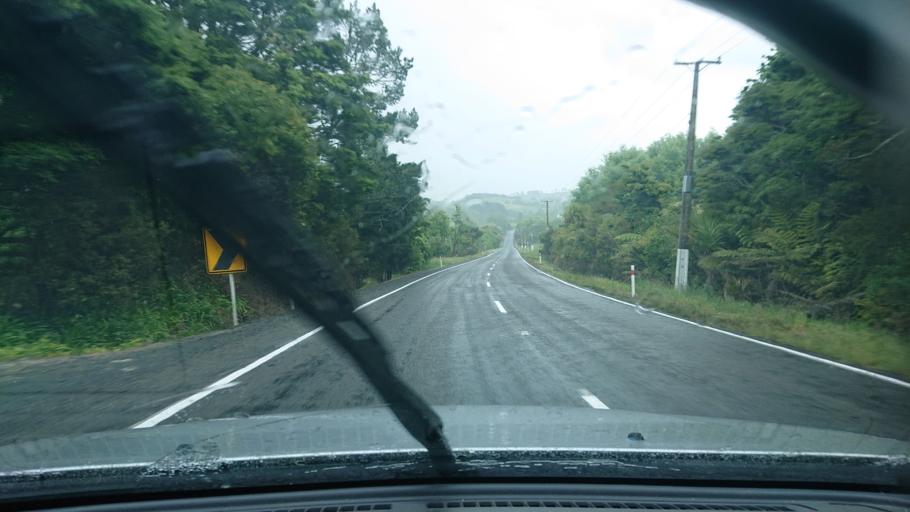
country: NZ
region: Auckland
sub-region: Auckland
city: Wellsford
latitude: -36.3140
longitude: 174.4947
